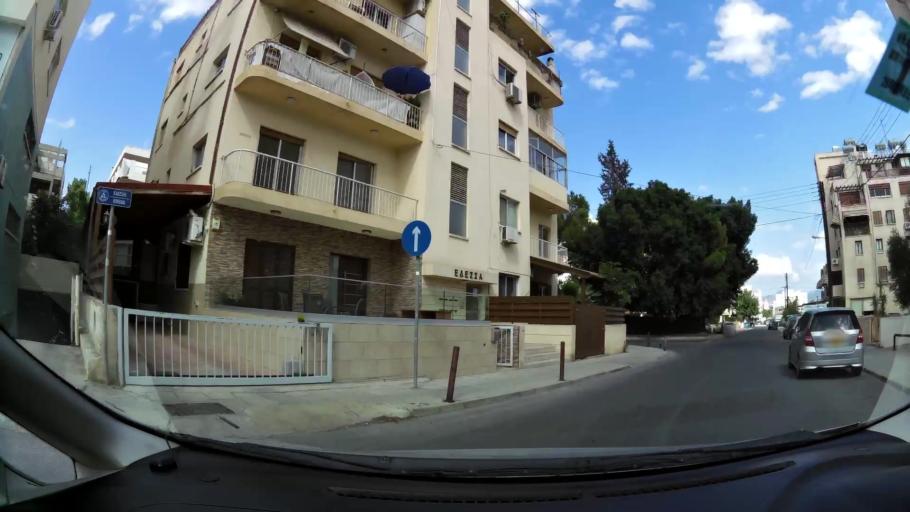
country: CY
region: Lefkosia
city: Nicosia
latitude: 35.1522
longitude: 33.3738
